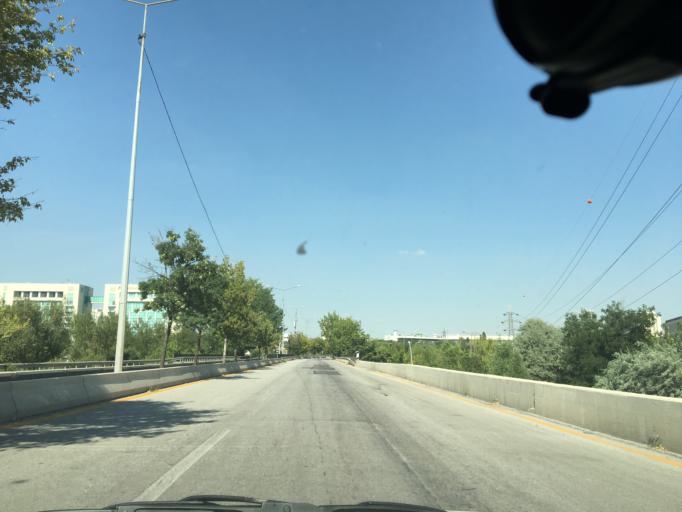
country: TR
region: Ankara
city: Ankara
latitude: 39.9183
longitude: 32.7993
